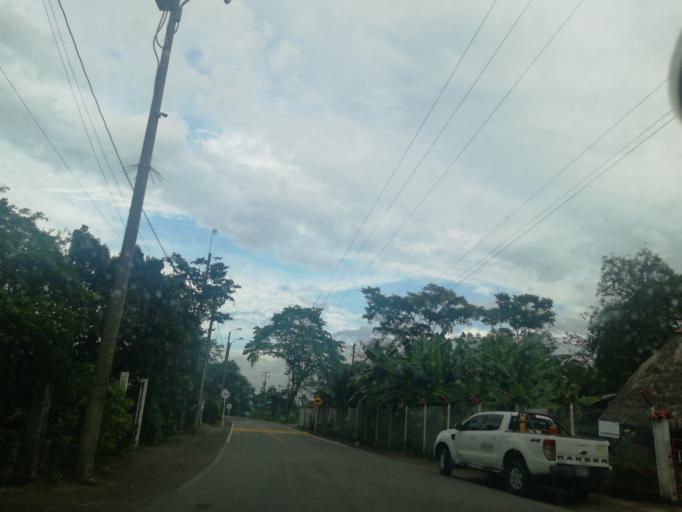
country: CO
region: Meta
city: Acacias
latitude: 3.9877
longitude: -73.7304
